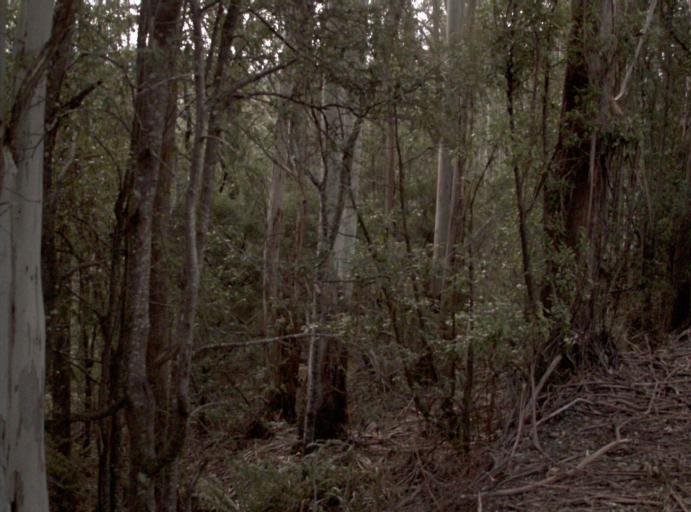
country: AU
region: Tasmania
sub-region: Dorset
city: Scottsdale
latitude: -41.2809
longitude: 147.3394
